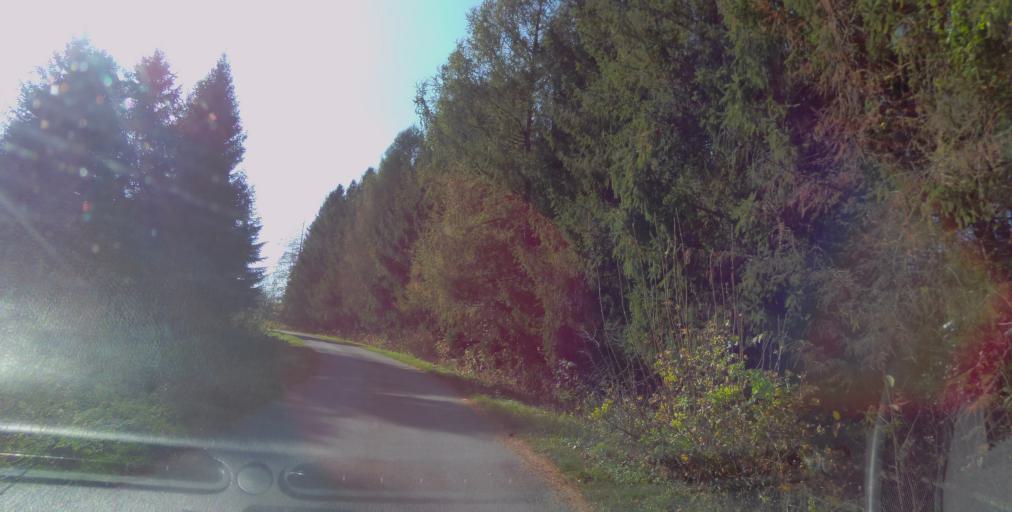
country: PL
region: Subcarpathian Voivodeship
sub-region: Powiat leski
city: Polanczyk
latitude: 49.3283
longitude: 22.4274
